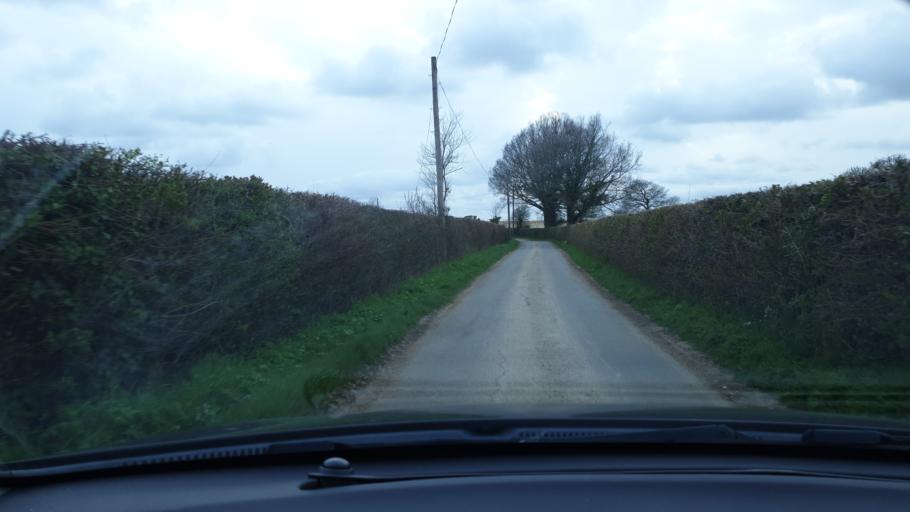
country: GB
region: England
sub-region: Essex
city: Mistley
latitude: 51.8971
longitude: 1.1344
